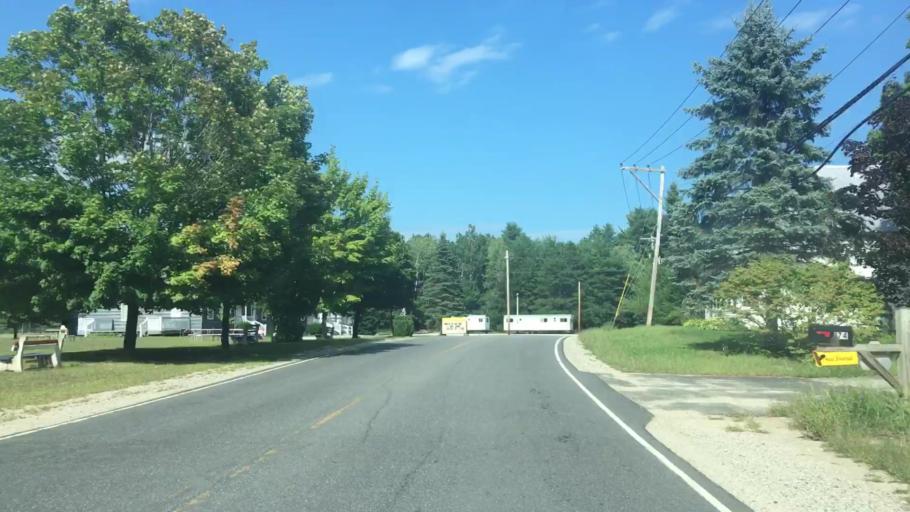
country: US
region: Maine
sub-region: Oxford County
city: Oxford
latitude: 44.1389
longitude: -70.4880
